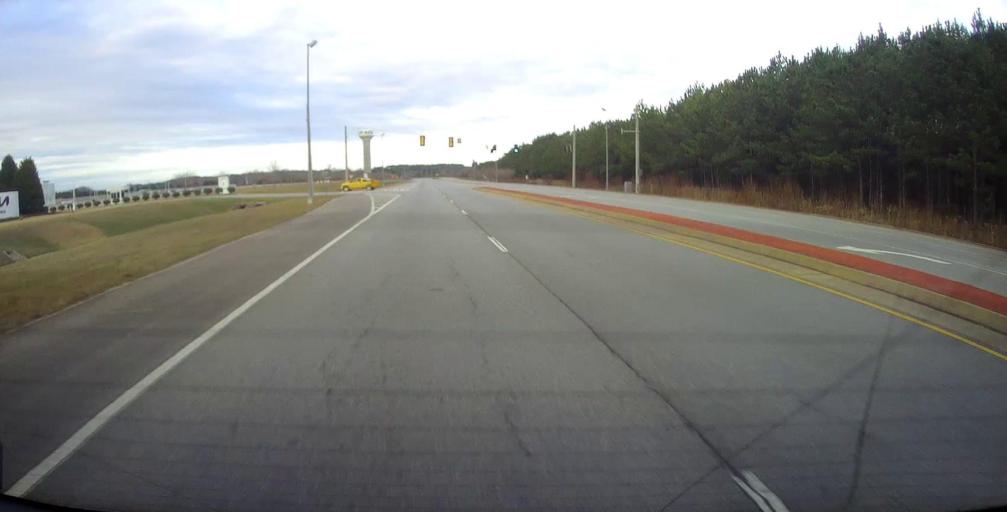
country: US
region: Georgia
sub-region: Troup County
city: West Point
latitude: 32.9155
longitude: -85.1180
